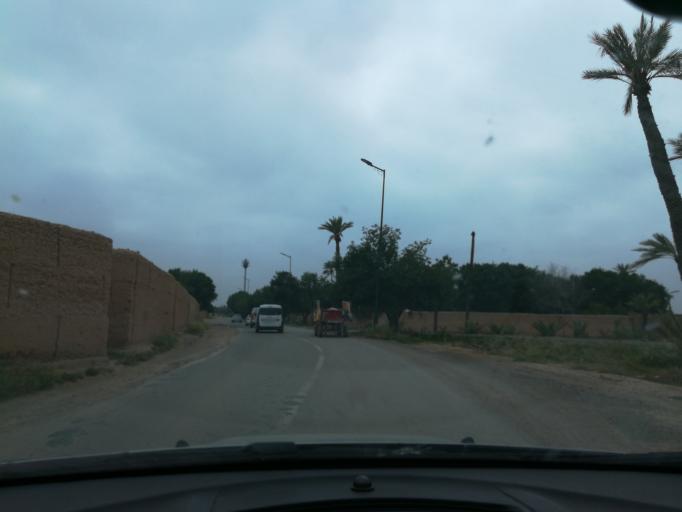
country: MA
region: Marrakech-Tensift-Al Haouz
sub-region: Marrakech
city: Marrakesh
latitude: 31.6625
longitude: -7.9690
